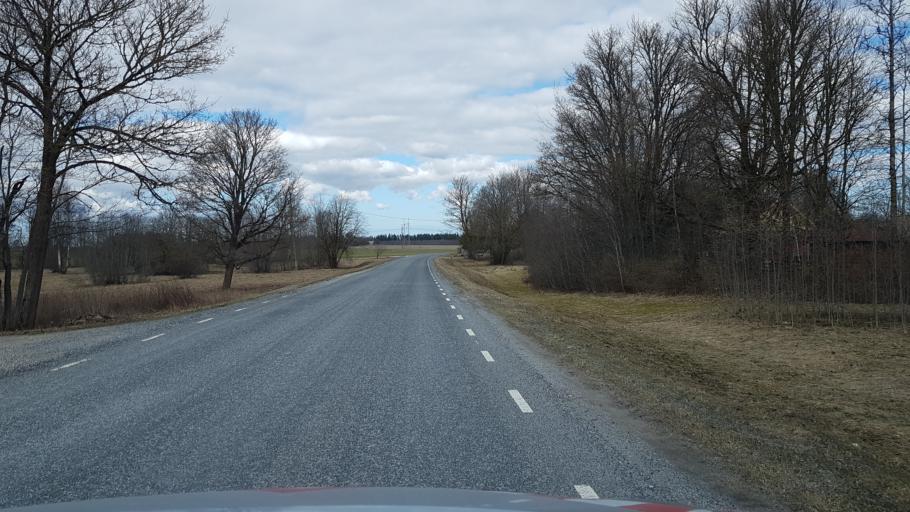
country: EE
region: Laeaene-Virumaa
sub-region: Tamsalu vald
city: Tamsalu
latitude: 59.1742
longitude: 26.1239
